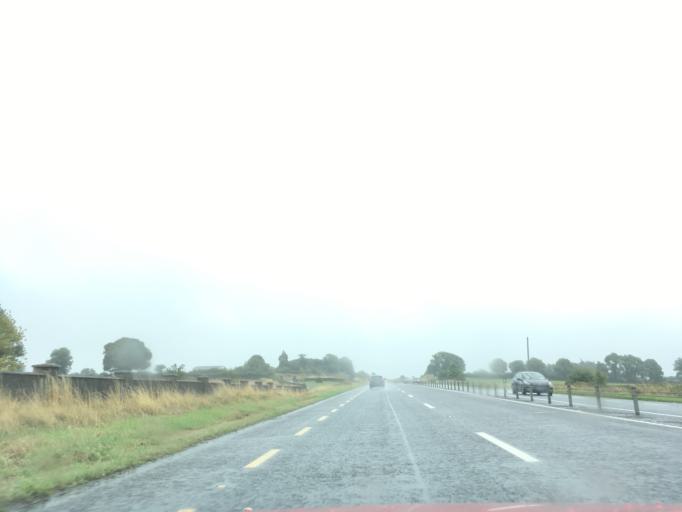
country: IE
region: Leinster
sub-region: Kilkenny
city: Piltown
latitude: 52.3566
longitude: -7.3569
